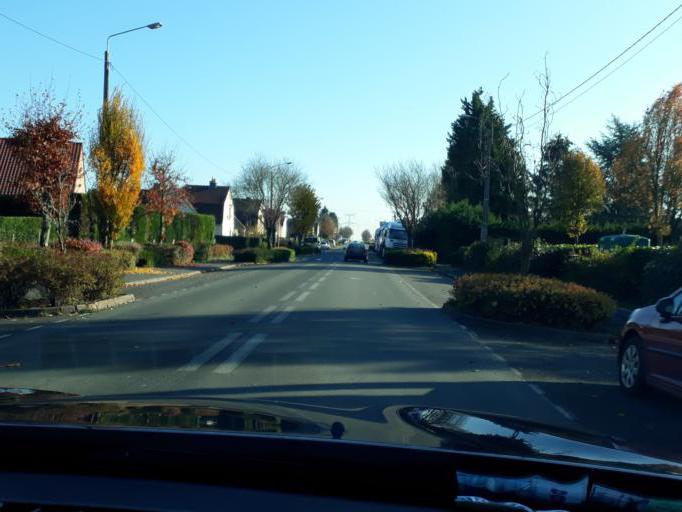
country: FR
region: Nord-Pas-de-Calais
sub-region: Departement du Nord
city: Aniche
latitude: 50.3147
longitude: 3.2678
